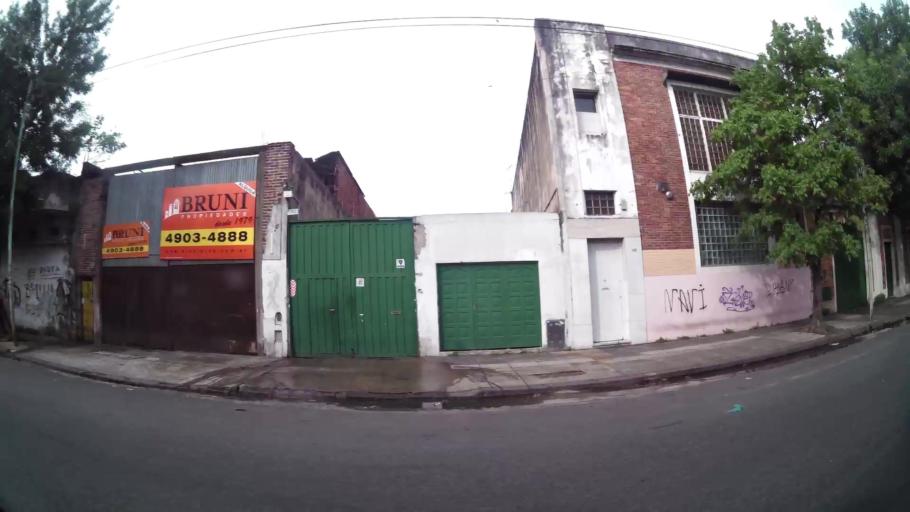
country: AR
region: Buenos Aires F.D.
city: Villa Lugano
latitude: -34.6463
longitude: -58.4306
